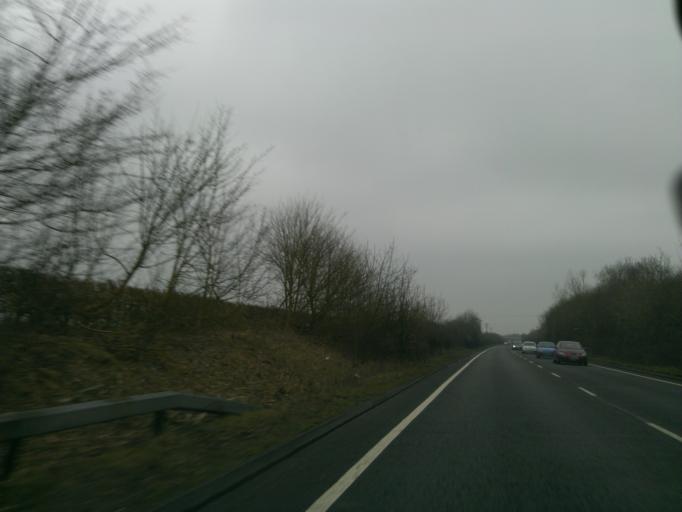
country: GB
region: England
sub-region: Essex
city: Little Clacton
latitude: 51.8294
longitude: 1.1303
